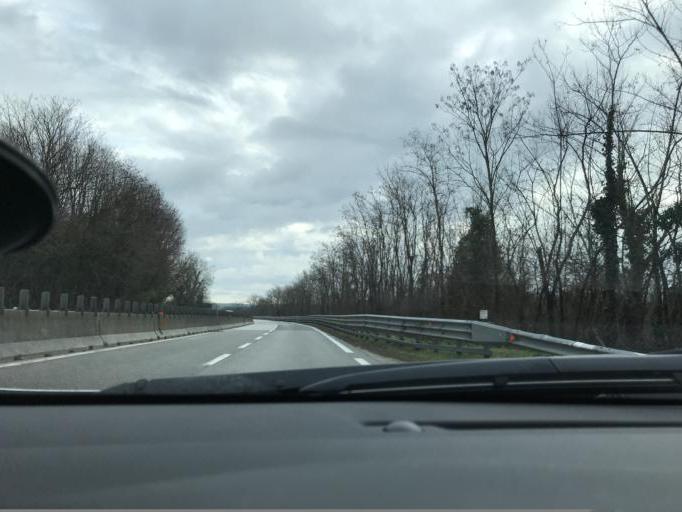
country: IT
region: The Marches
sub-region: Provincia di Ancona
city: Pianello Vallesina
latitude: 43.4873
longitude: 13.1921
